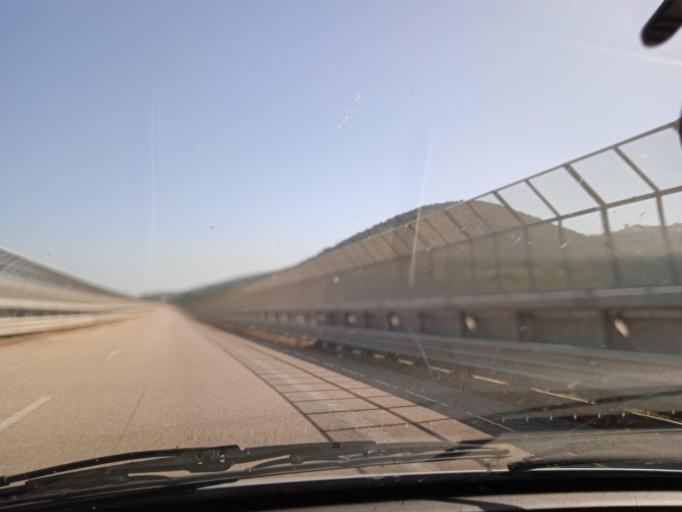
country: IT
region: Sicily
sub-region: Messina
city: Rocca di Capri Leone
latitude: 38.1063
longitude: 14.7207
